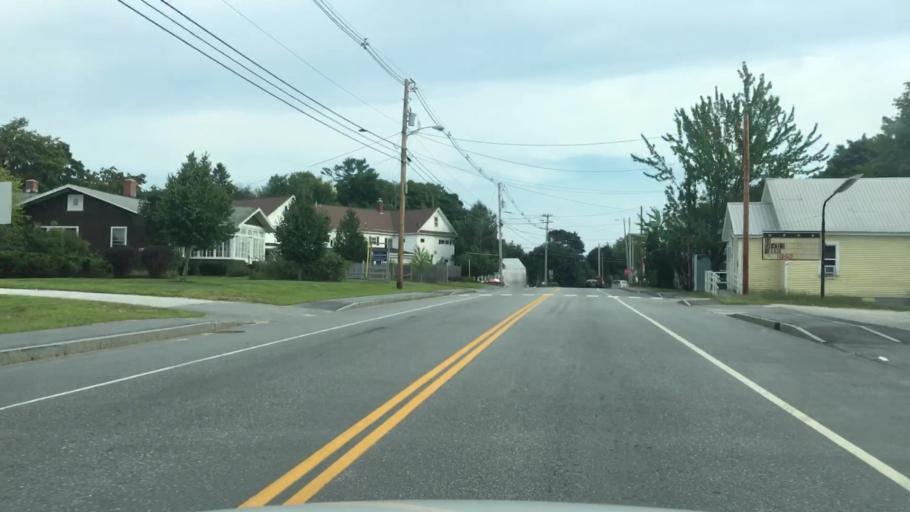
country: US
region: Maine
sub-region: Oxford County
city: Norway
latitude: 44.2087
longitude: -70.5324
